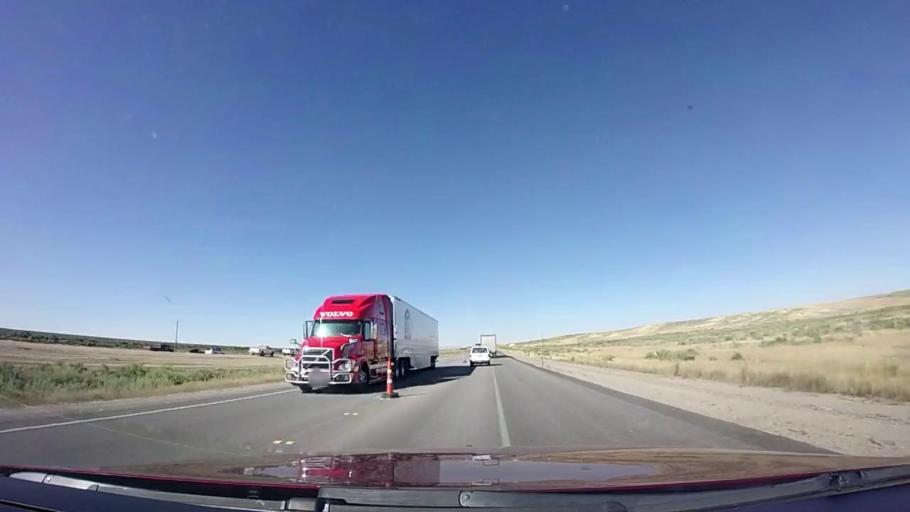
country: US
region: Wyoming
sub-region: Carbon County
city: Rawlins
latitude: 41.7024
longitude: -107.9046
